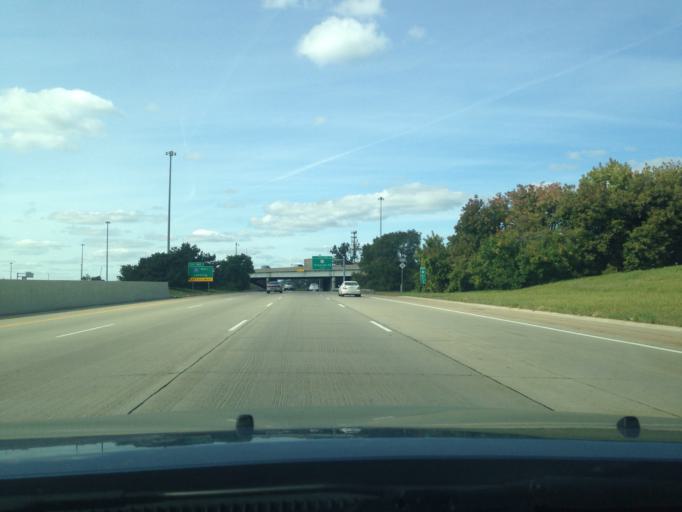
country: US
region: Michigan
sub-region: Oakland County
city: Bingham Farms
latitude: 42.4847
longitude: -83.2642
